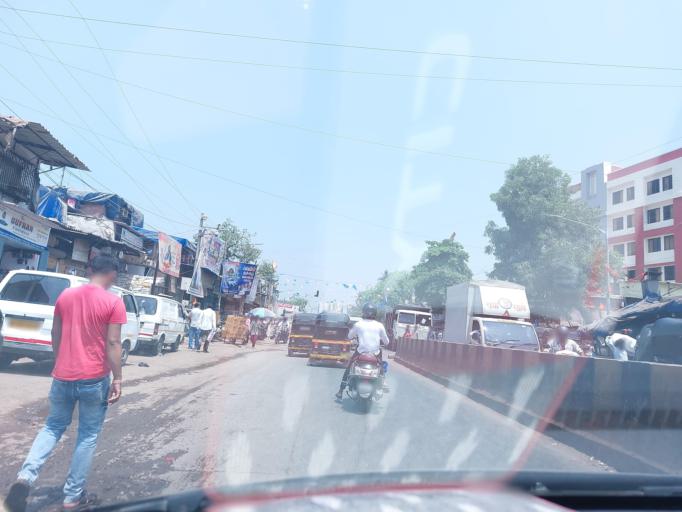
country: IN
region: Maharashtra
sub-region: Mumbai Suburban
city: Mumbai
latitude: 19.0579
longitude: 72.8865
